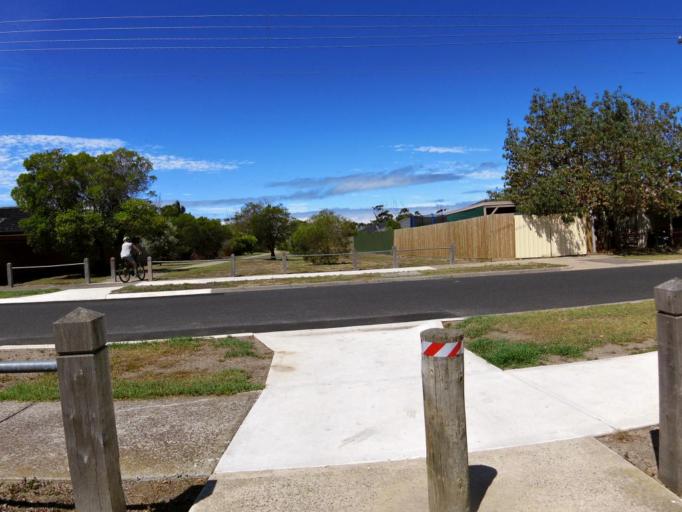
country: AU
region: Victoria
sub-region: Hobsons Bay
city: Altona Meadows
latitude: -37.8813
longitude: 144.7910
